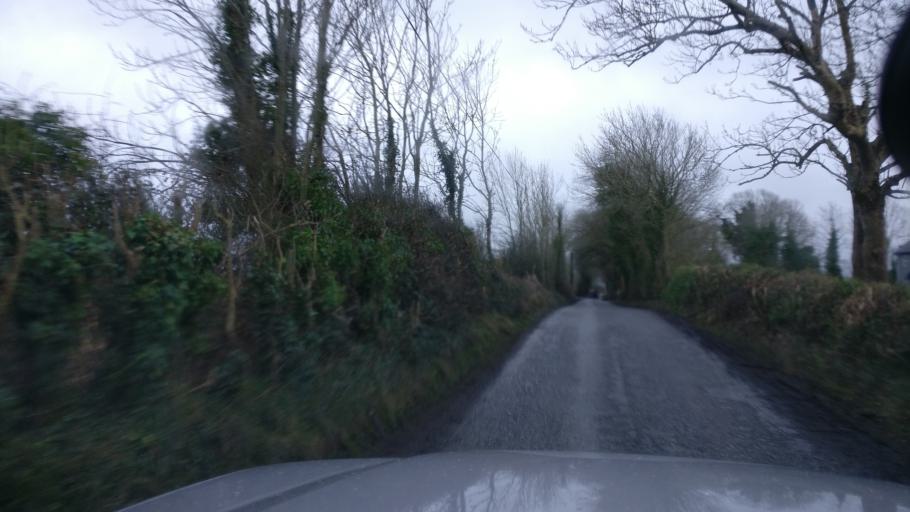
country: IE
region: Connaught
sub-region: County Galway
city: Loughrea
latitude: 53.1968
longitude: -8.6632
